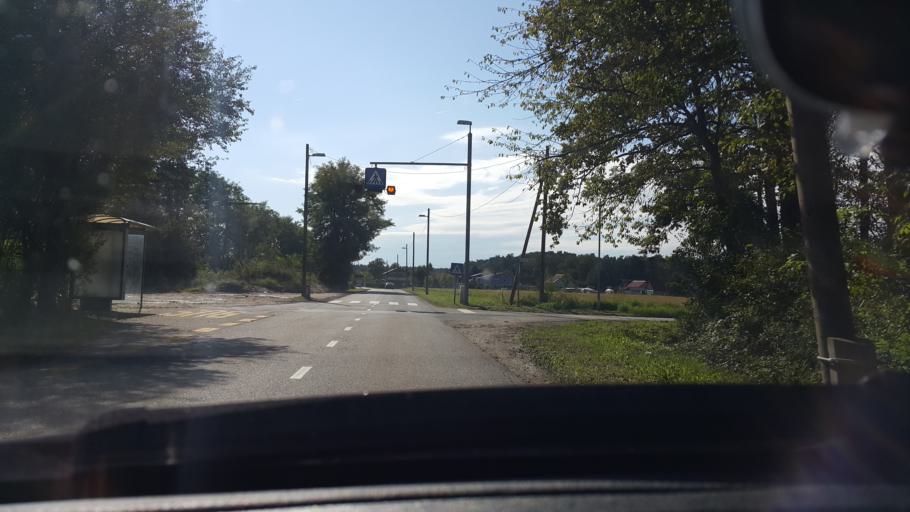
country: SI
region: Race-Fram
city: Race
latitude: 46.4703
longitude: 15.7114
